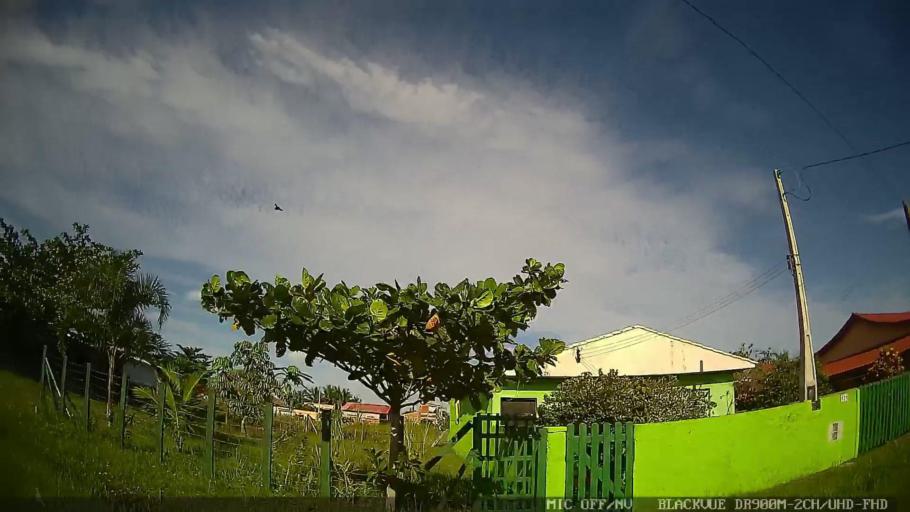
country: BR
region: Sao Paulo
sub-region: Iguape
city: Iguape
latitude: -24.7631
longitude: -47.5762
